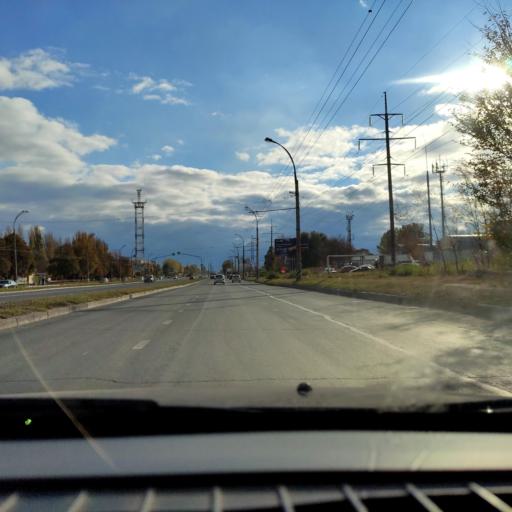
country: RU
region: Samara
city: Tol'yatti
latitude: 53.5344
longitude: 49.2623
